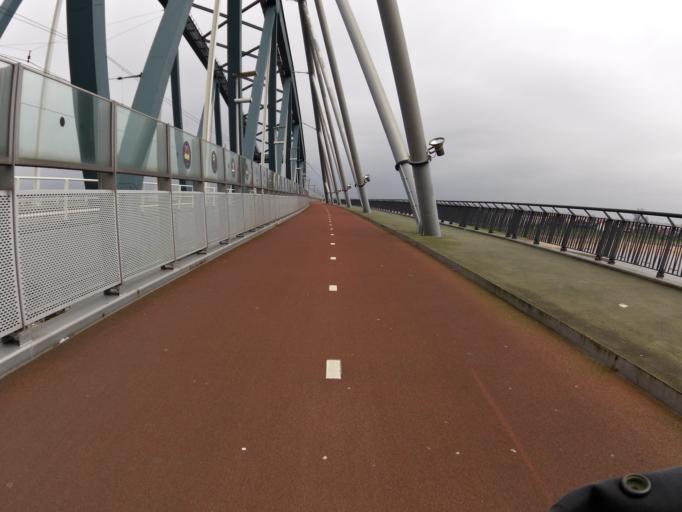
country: NL
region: Gelderland
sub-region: Gemeente Nijmegen
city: Nijmegen
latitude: 51.8517
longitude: 5.8567
